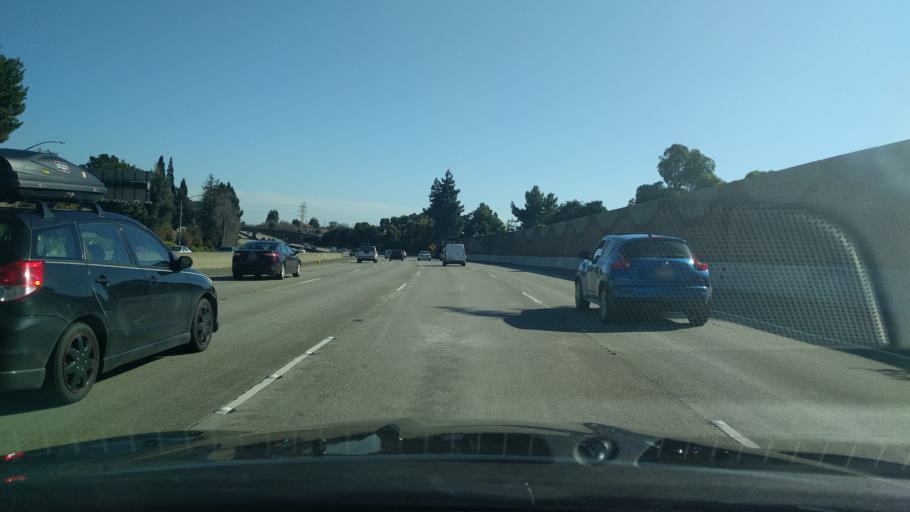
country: US
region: California
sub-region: Alameda County
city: San Leandro
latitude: 37.7262
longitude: -122.1380
